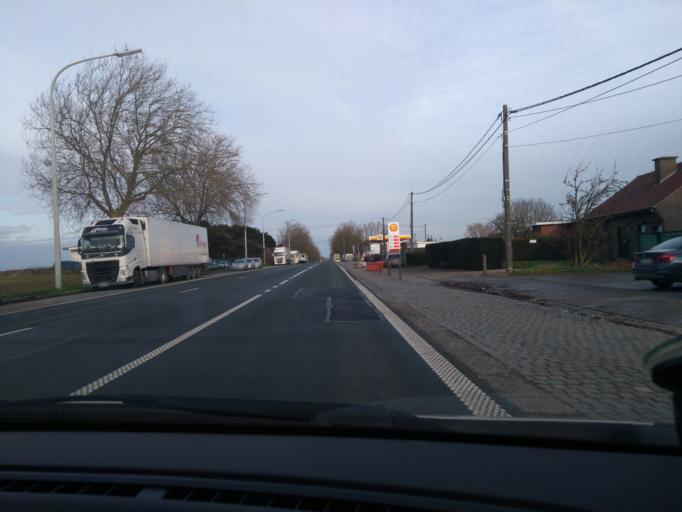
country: BE
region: Wallonia
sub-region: Province du Hainaut
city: Quevy-le-Petit
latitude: 50.3443
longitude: 3.9703
